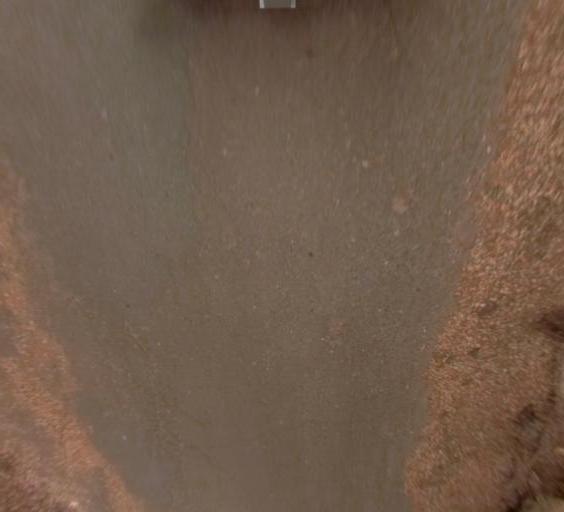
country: US
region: California
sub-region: Madera County
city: Oakhurst
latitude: 37.3653
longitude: -119.6023
